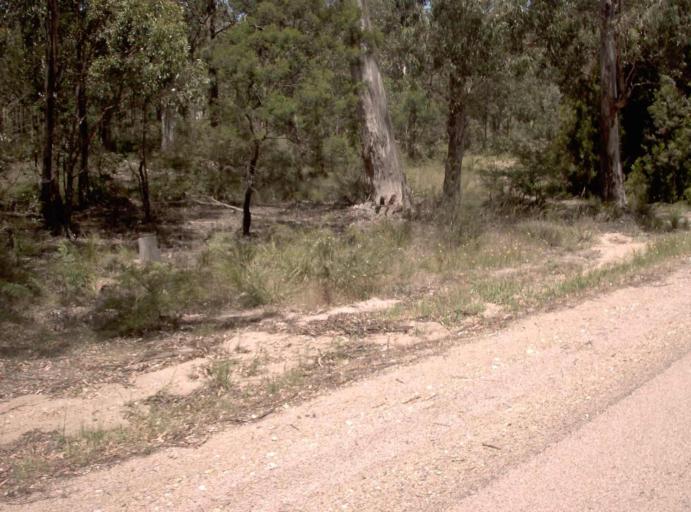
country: AU
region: Victoria
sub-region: East Gippsland
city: Bairnsdale
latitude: -37.7439
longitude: 147.7622
